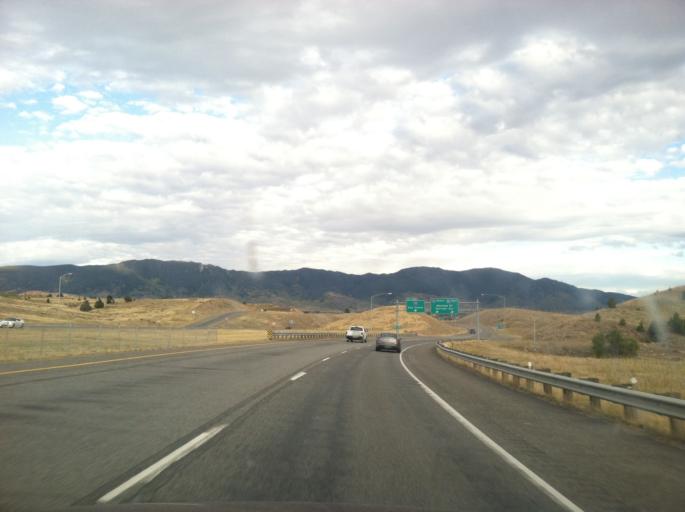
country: US
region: Montana
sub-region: Silver Bow County
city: Butte
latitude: 46.0051
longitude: -112.5756
